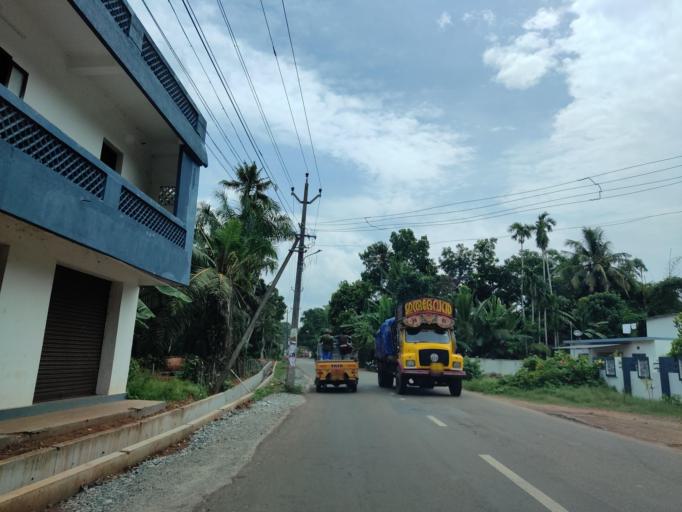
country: IN
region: Kerala
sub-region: Alappuzha
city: Mavelikara
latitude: 9.2260
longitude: 76.6191
